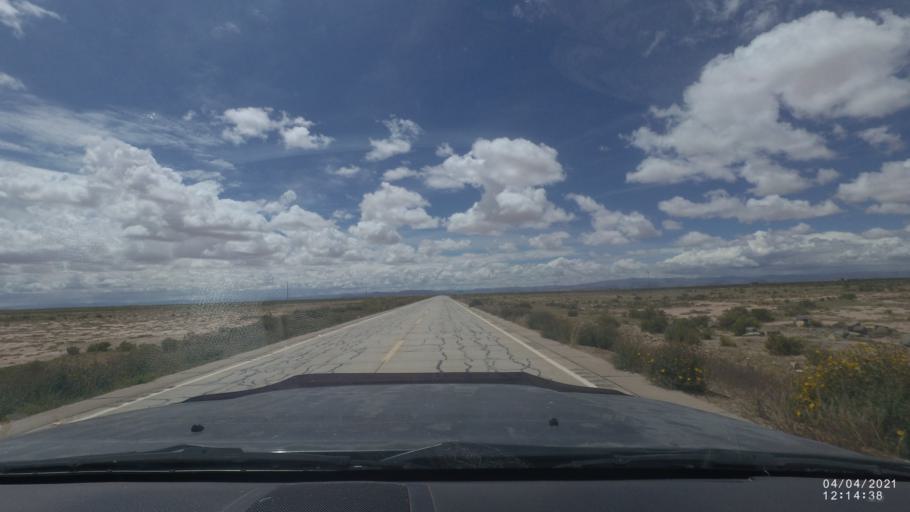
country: BO
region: Oruro
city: Oruro
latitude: -18.1314
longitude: -67.3253
